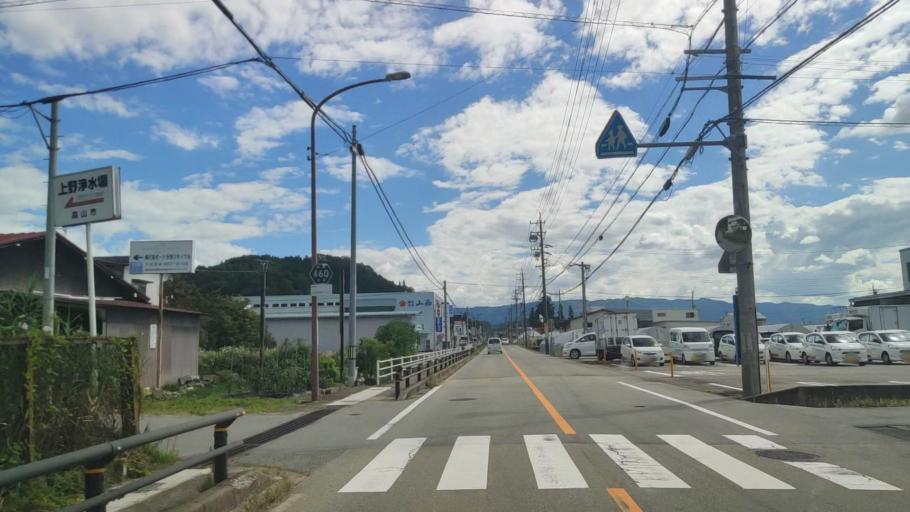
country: JP
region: Gifu
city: Takayama
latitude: 36.1689
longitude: 137.2469
